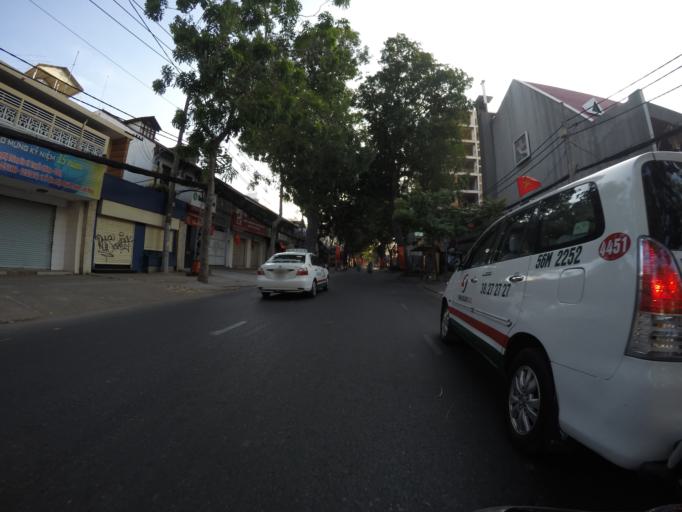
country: VN
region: Ho Chi Minh City
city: Quan Mot
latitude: 10.7897
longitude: 106.7006
